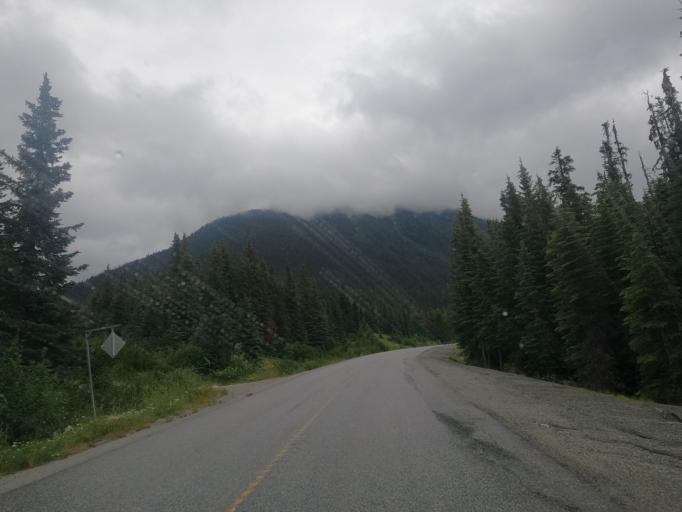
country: CA
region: British Columbia
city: Pemberton
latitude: 50.3864
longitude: -122.4662
